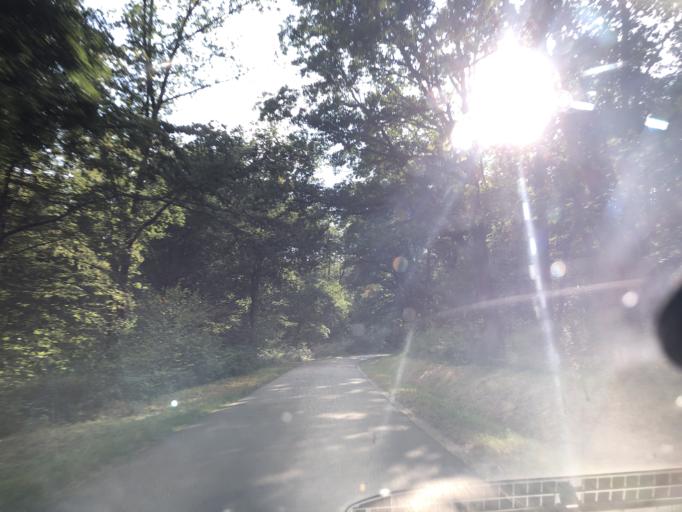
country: FR
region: Bourgogne
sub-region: Departement de l'Yonne
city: Saint-Georges-sur-Baulche
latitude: 47.8198
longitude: 3.5058
